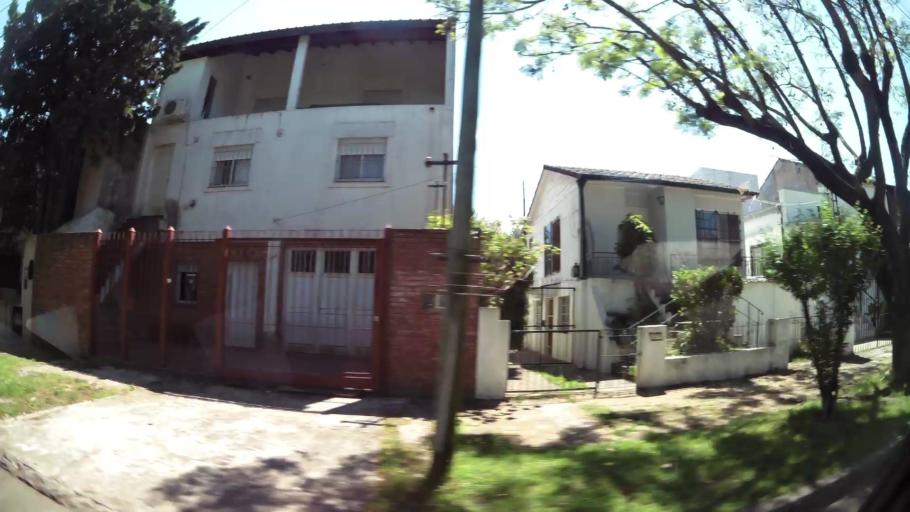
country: AR
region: Buenos Aires
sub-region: Partido de Tigre
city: Tigre
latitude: -34.4274
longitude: -58.5710
